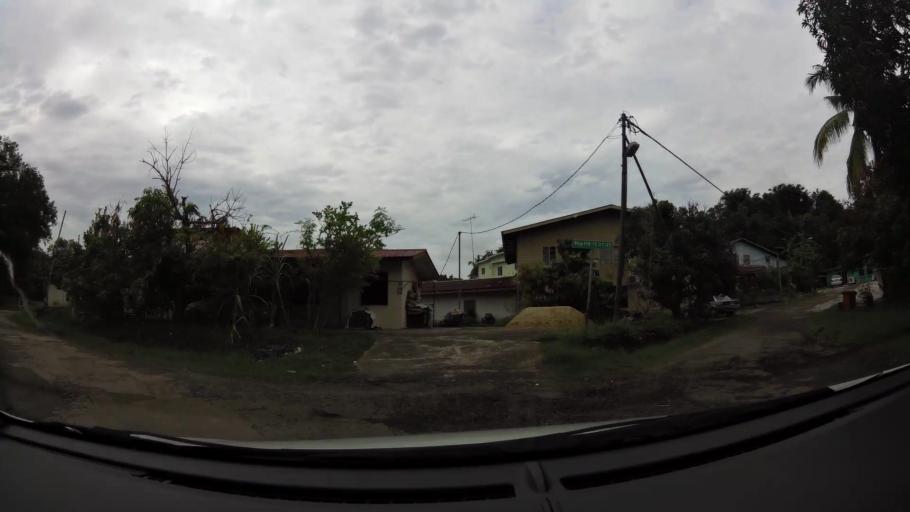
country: BN
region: Brunei and Muara
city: Bandar Seri Begawan
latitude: 4.8970
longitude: 114.9312
